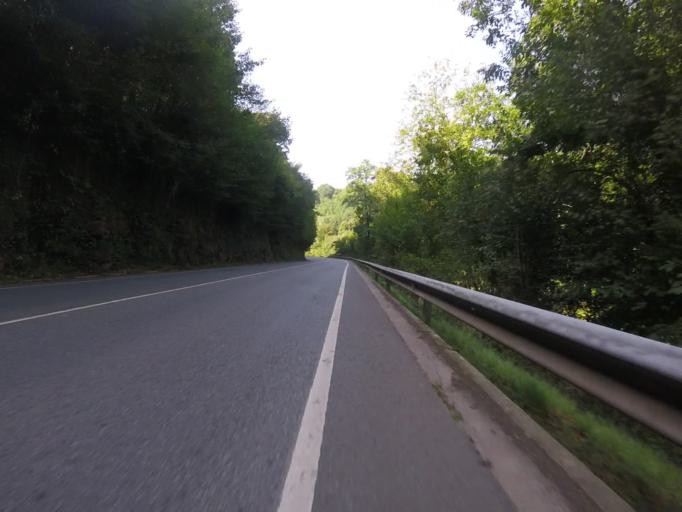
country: ES
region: Navarre
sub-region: Provincia de Navarra
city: Zugarramurdi
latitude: 43.1656
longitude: -1.4948
